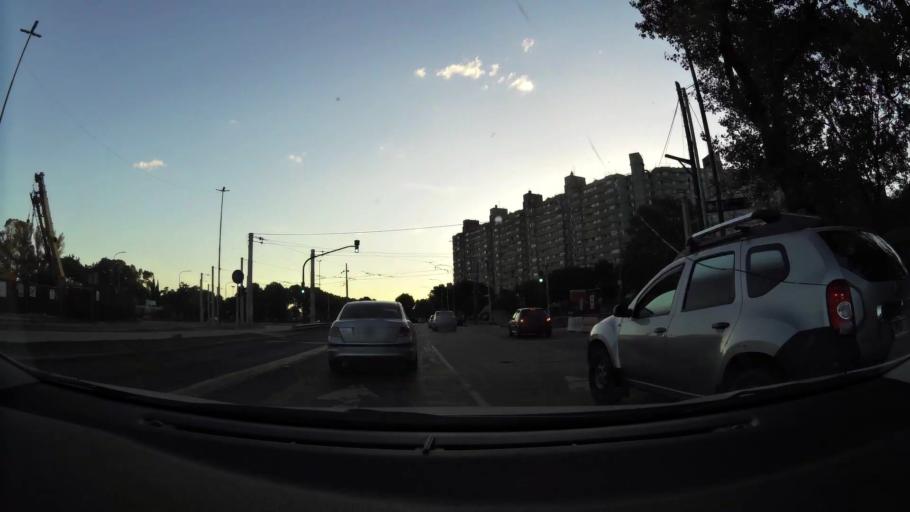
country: AR
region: Buenos Aires F.D.
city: Villa Lugano
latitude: -34.6861
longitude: -58.4574
